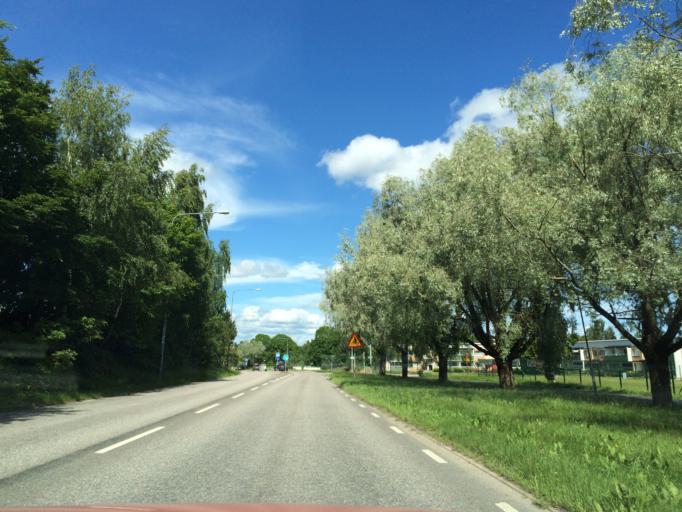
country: SE
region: Vaestra Goetaland
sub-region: Trollhattan
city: Trollhattan
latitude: 58.2866
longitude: 12.3288
